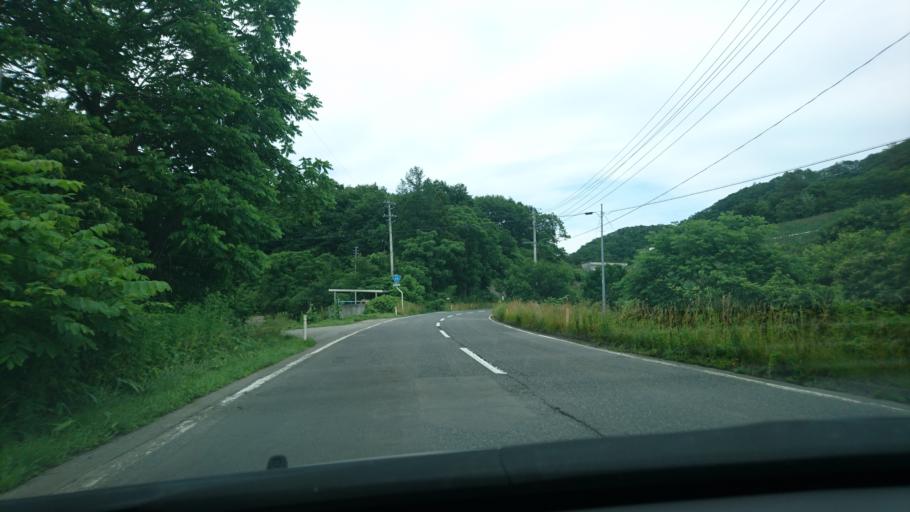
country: JP
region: Iwate
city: Miyako
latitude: 39.9815
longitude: 141.8585
